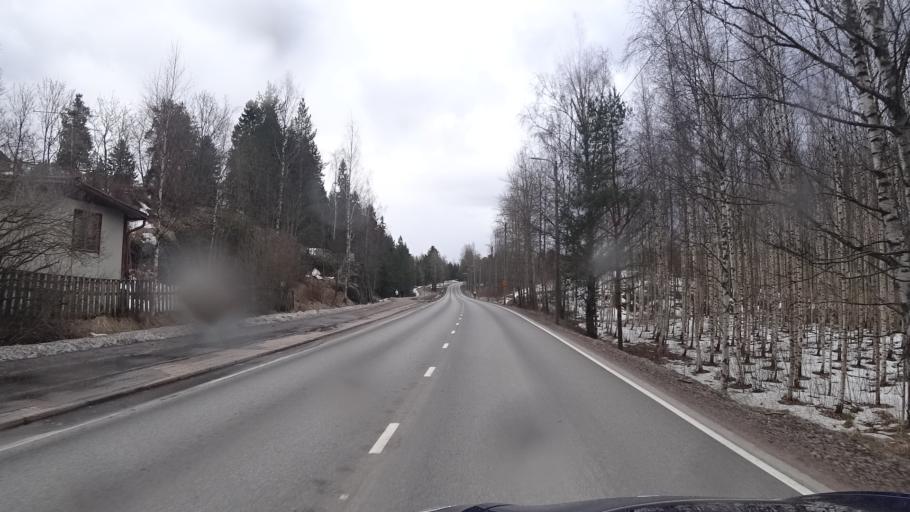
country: FI
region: Kymenlaakso
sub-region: Kotka-Hamina
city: Karhula
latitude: 60.5261
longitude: 26.9003
